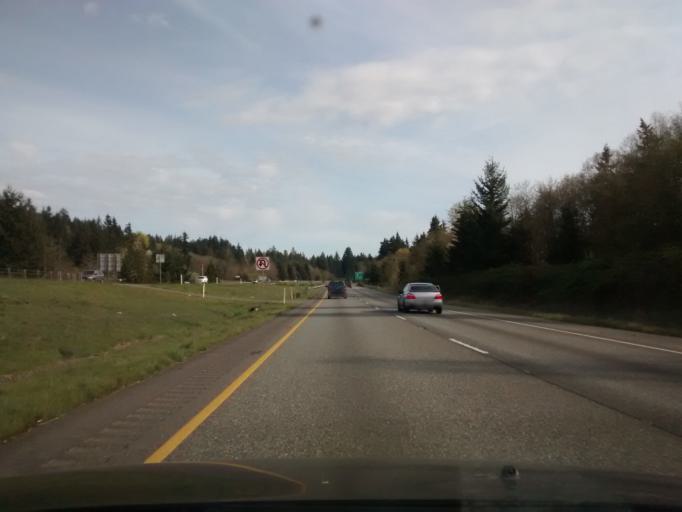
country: US
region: Washington
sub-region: Kitsap County
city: Silverdale
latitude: 47.6519
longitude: -122.7059
